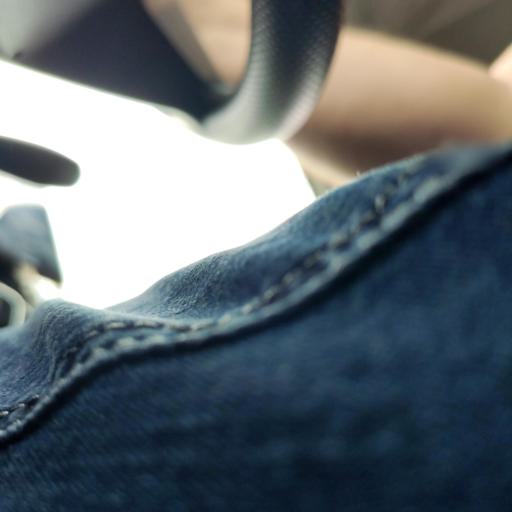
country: RU
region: Samara
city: Smyshlyayevka
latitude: 53.2227
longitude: 50.3450
